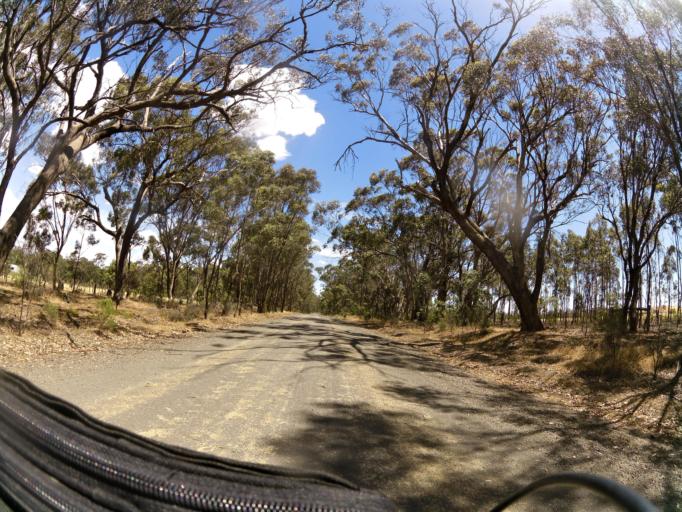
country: AU
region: Victoria
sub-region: Campaspe
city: Kyabram
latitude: -36.7977
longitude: 145.0798
